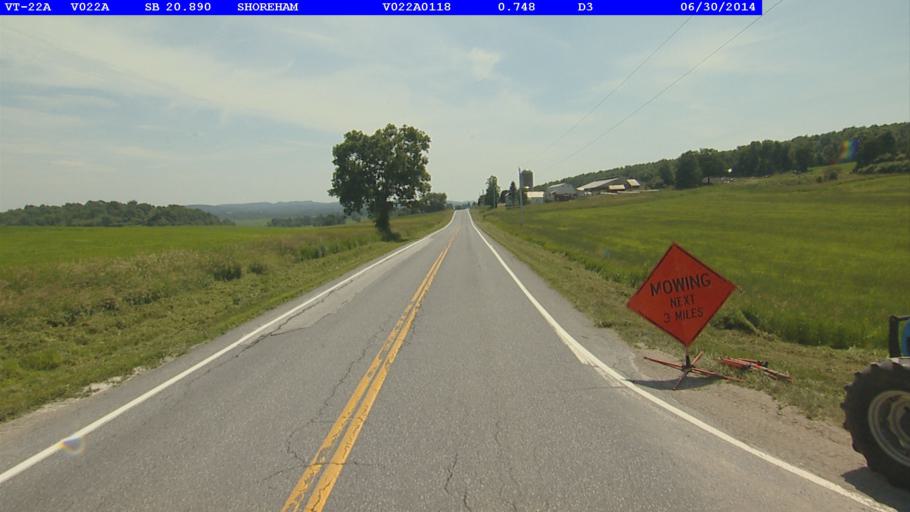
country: US
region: New York
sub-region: Essex County
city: Ticonderoga
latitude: 43.8602
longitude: -73.3095
